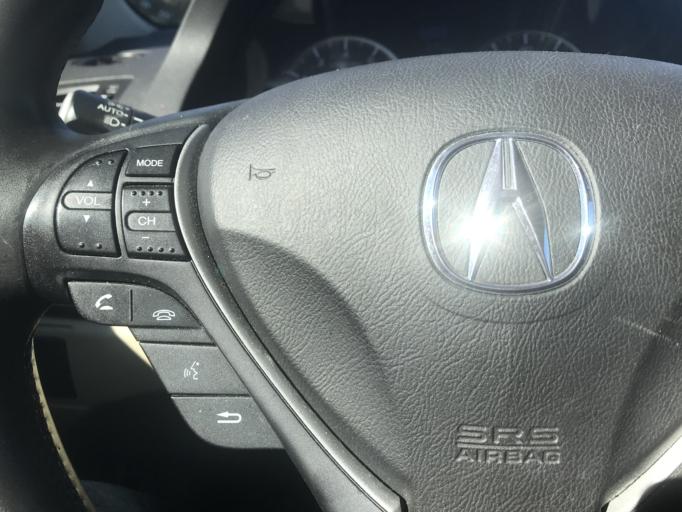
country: US
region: Louisiana
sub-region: Orleans Parish
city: New Orleans
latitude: 29.9521
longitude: -90.0909
